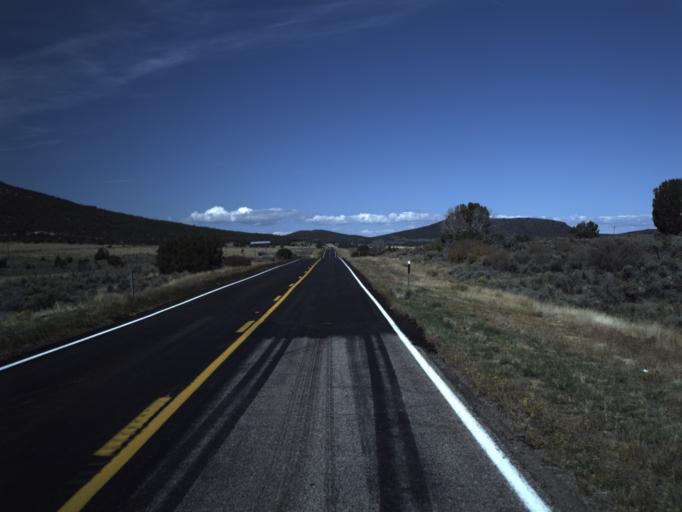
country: US
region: Utah
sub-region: Washington County
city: Enterprise
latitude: 37.4922
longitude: -113.6303
